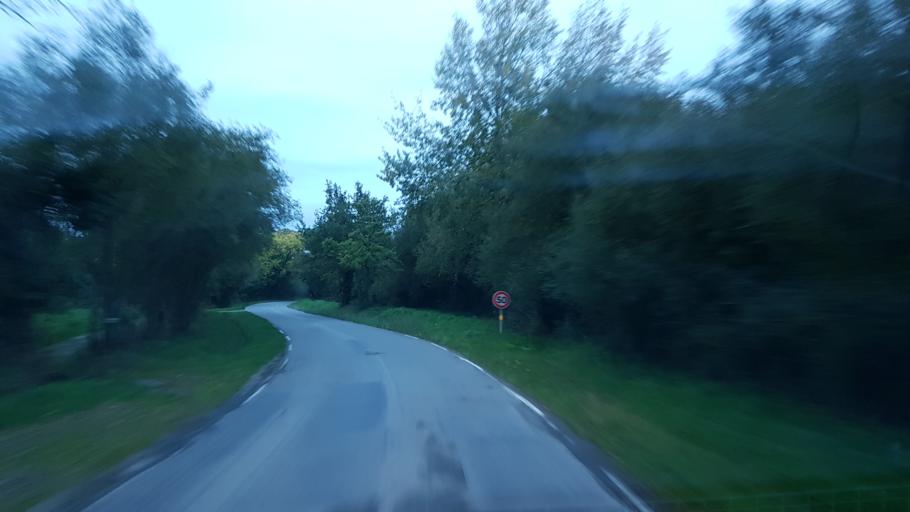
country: FR
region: Brittany
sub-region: Departement du Morbihan
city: Sarzeau
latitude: 47.5311
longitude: -2.7740
